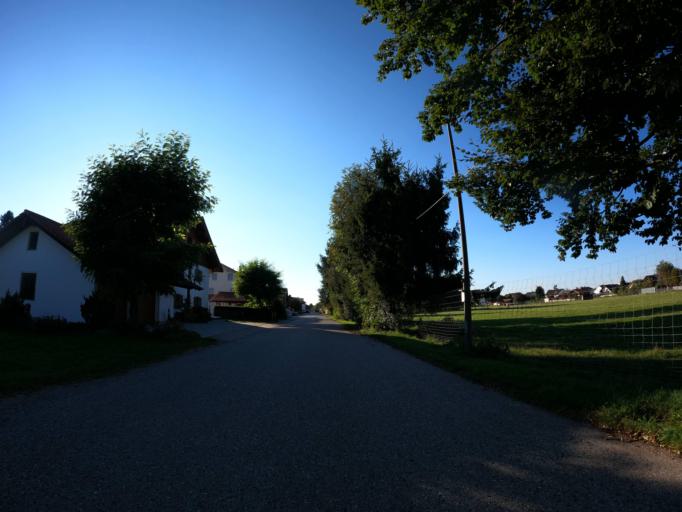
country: DE
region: Bavaria
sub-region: Upper Bavaria
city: Grasbrunn
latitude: 48.0567
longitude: 11.7758
